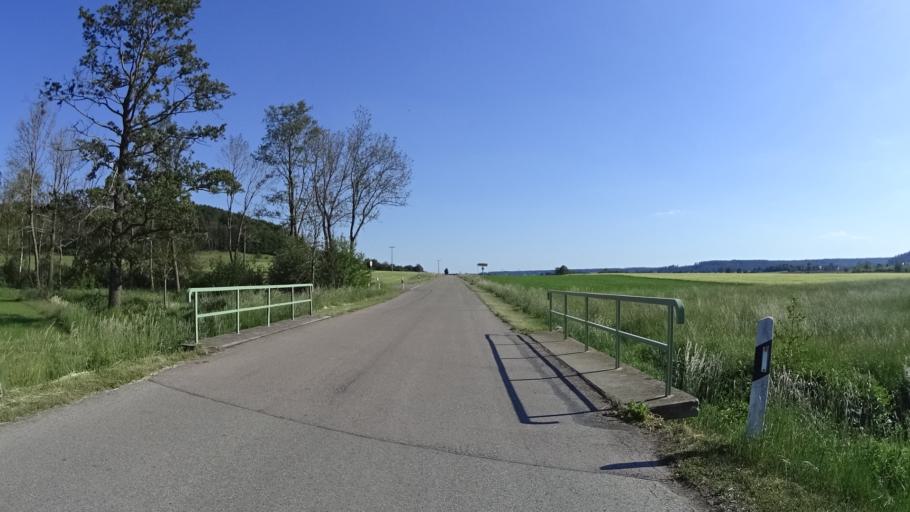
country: DE
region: Bavaria
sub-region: Regierungsbezirk Mittelfranken
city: Feuchtwangen
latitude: 49.2019
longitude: 10.3267
